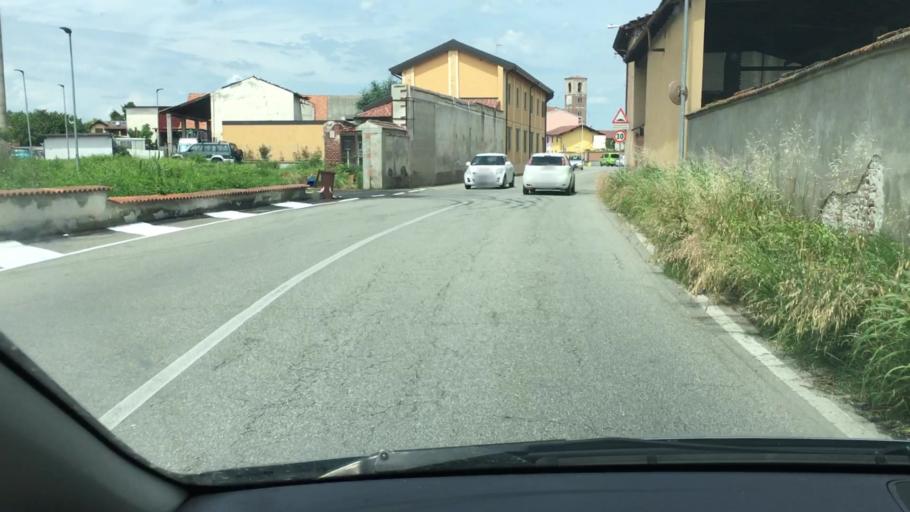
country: IT
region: Piedmont
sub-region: Provincia di Novara
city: Casalbeltrame
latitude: 45.4339
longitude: 8.4680
